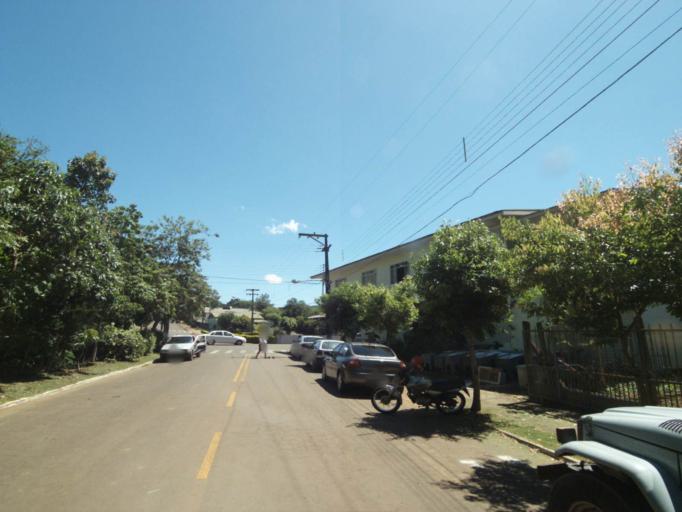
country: BR
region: Parana
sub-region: Ampere
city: Ampere
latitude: -26.1732
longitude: -53.3602
